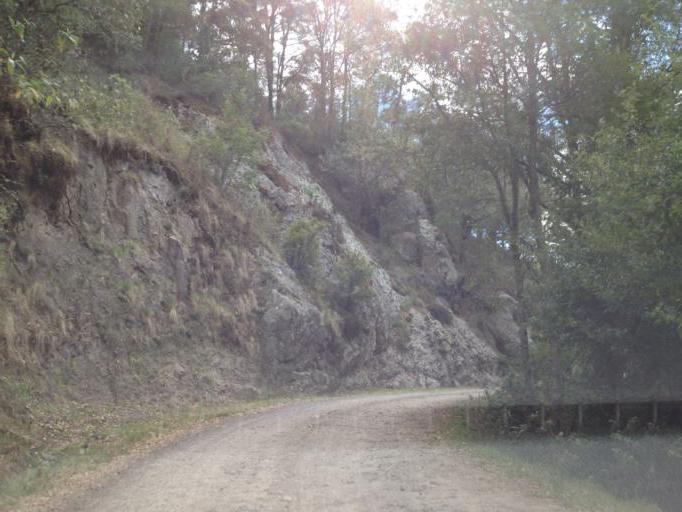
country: MX
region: Hidalgo
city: Mineral del Monte
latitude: 20.2091
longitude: -98.6776
